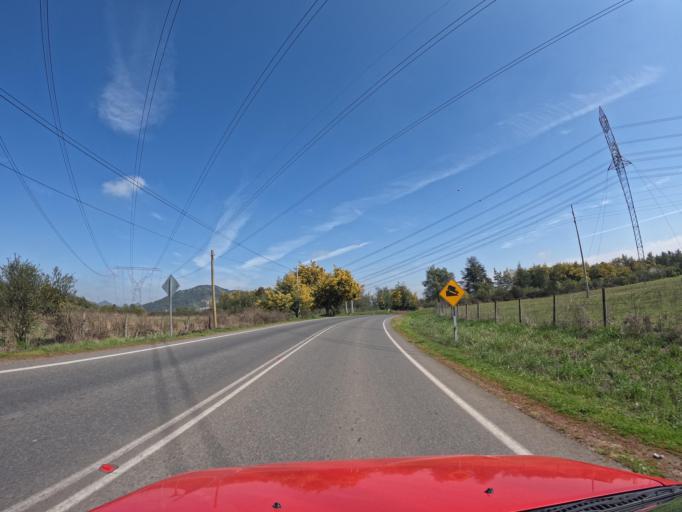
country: CL
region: Maule
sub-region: Provincia de Talca
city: San Clemente
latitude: -35.4885
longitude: -71.2856
